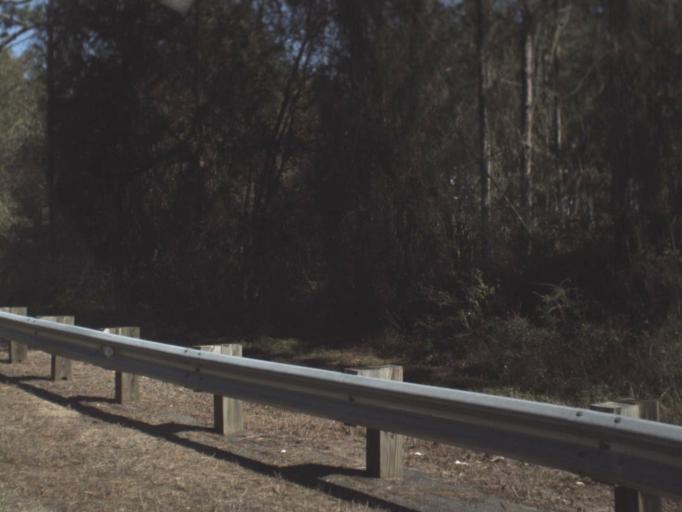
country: US
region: Florida
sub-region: Franklin County
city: Carrabelle
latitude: 29.9139
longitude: -84.5271
